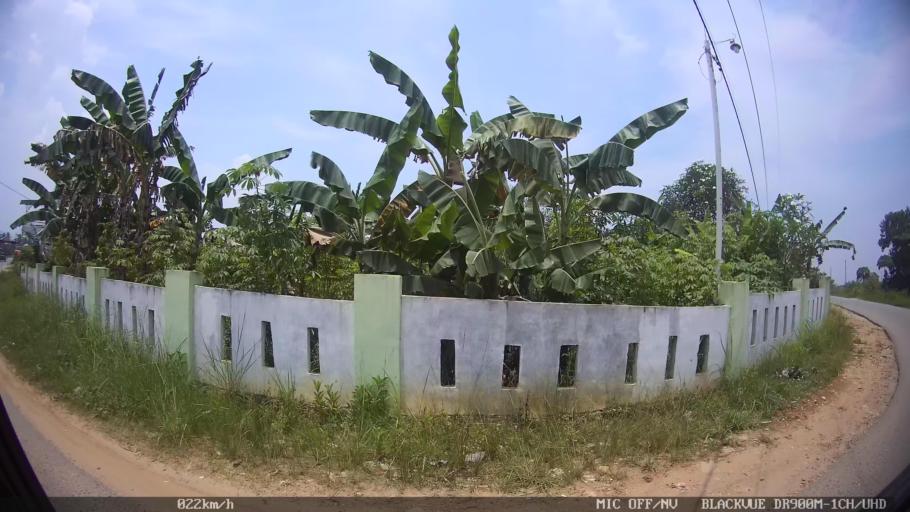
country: ID
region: Lampung
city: Kedaton
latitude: -5.3302
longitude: 105.2461
